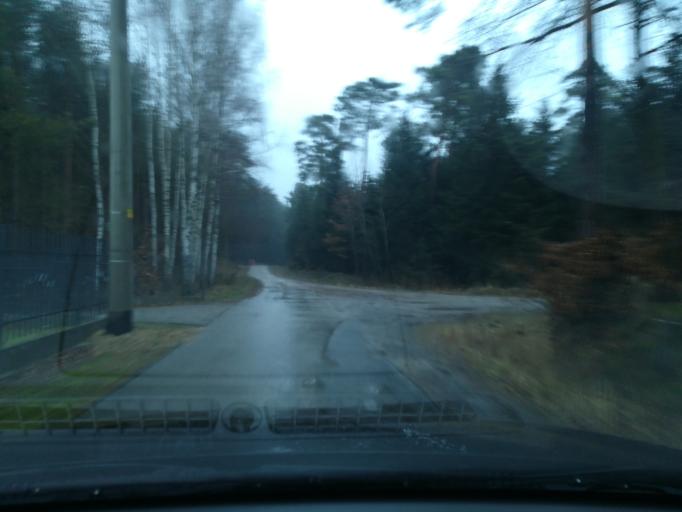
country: PL
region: Subcarpathian Voivodeship
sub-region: Powiat lancucki
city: Bialobrzegi
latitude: 50.1236
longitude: 22.3652
